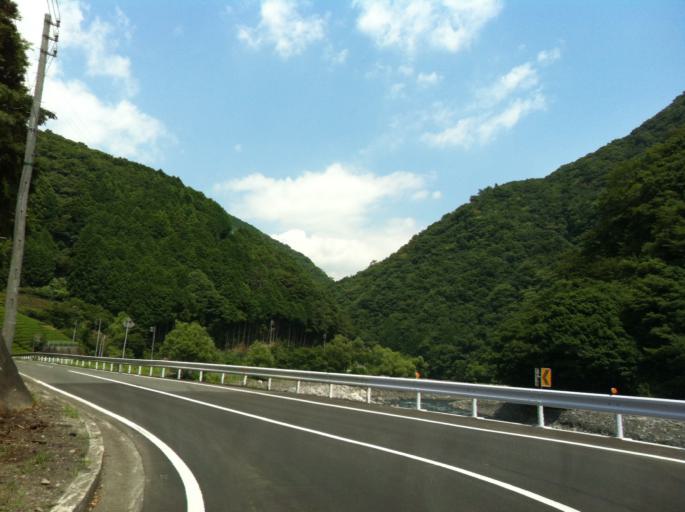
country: JP
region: Shizuoka
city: Shizuoka-shi
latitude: 35.2145
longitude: 138.3513
